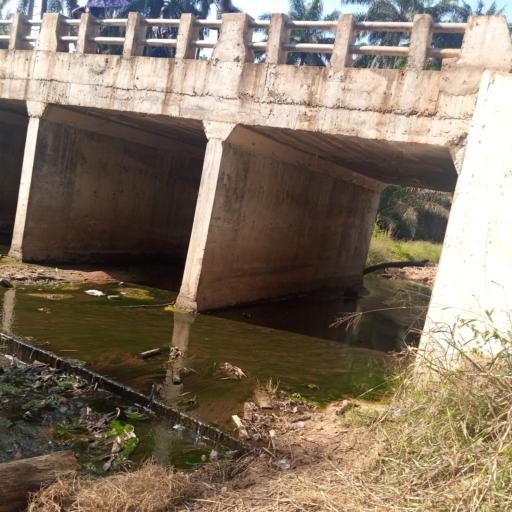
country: NG
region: Osun
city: Modakeke
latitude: 7.1718
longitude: 4.3511
